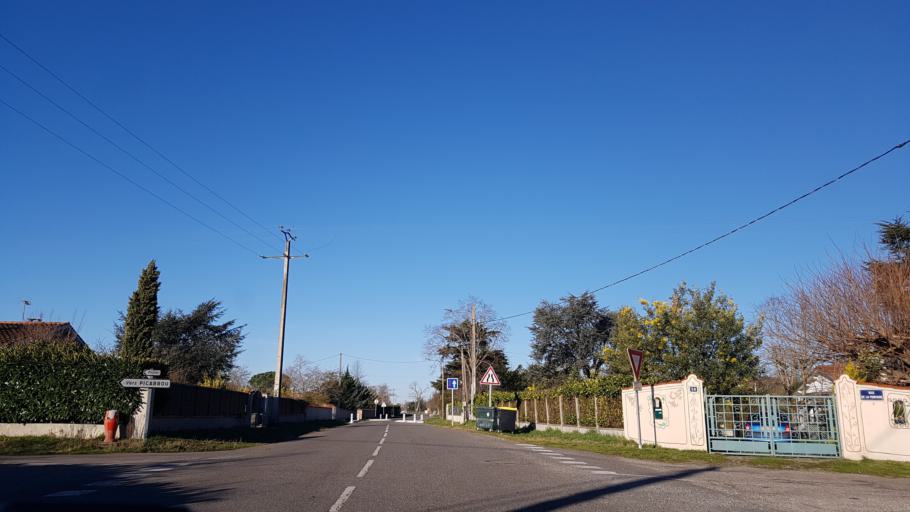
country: FR
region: Midi-Pyrenees
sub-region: Departement de la Haute-Garonne
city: Calmont
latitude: 43.2875
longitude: 1.6210
